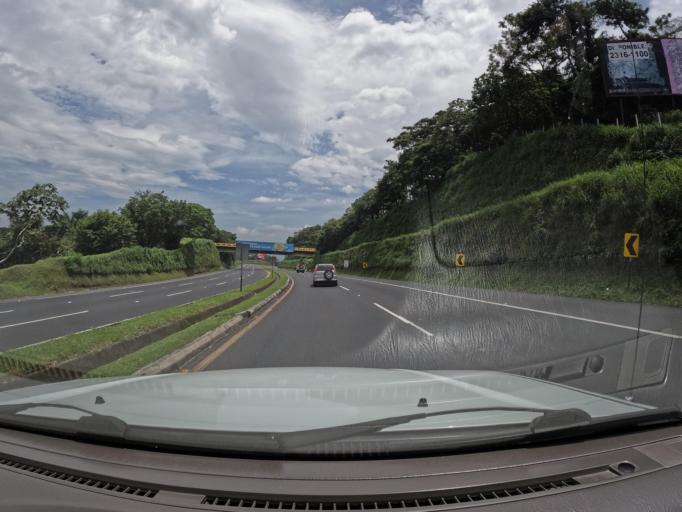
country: GT
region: Escuintla
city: Palin
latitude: 14.3946
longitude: -90.7388
